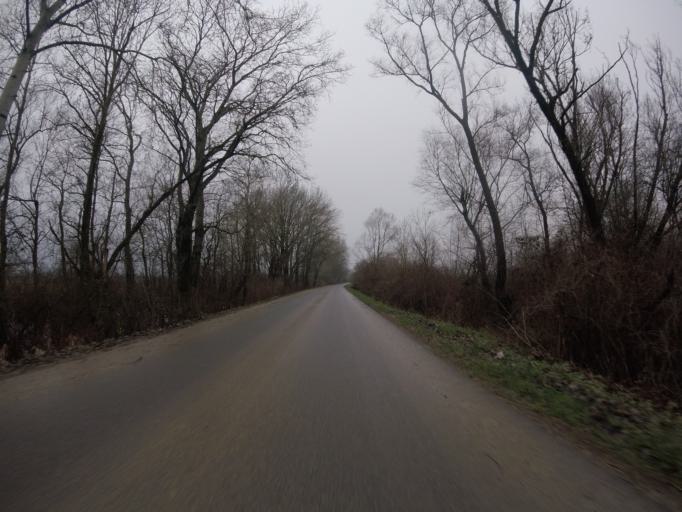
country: HR
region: Sisacko-Moslavacka
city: Lekenik
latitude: 45.6243
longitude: 16.3232
